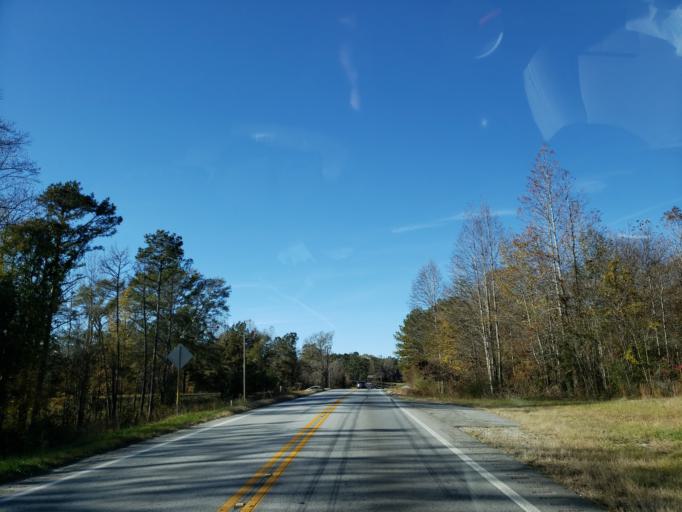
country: US
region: Alabama
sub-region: Calhoun County
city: Choccolocco
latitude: 33.5734
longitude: -85.6682
